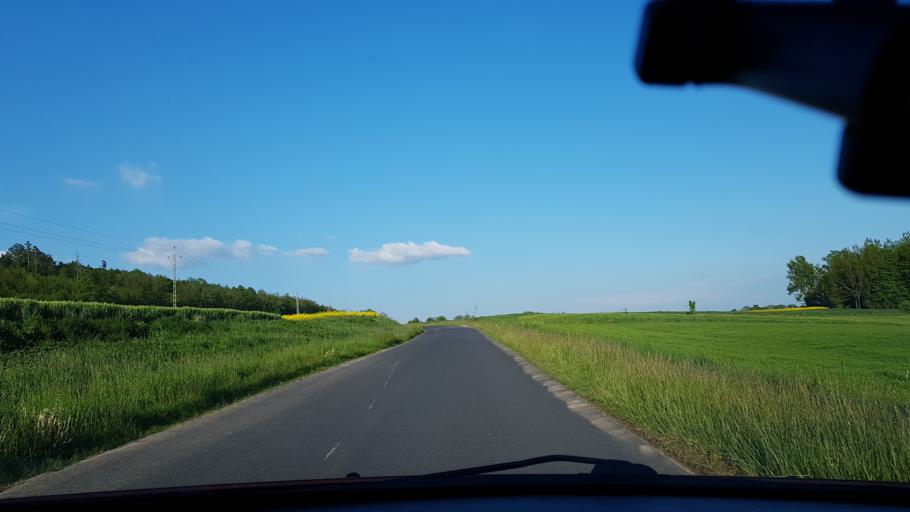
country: PL
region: Lower Silesian Voivodeship
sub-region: Powiat zabkowicki
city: Budzow
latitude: 50.6128
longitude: 16.6792
